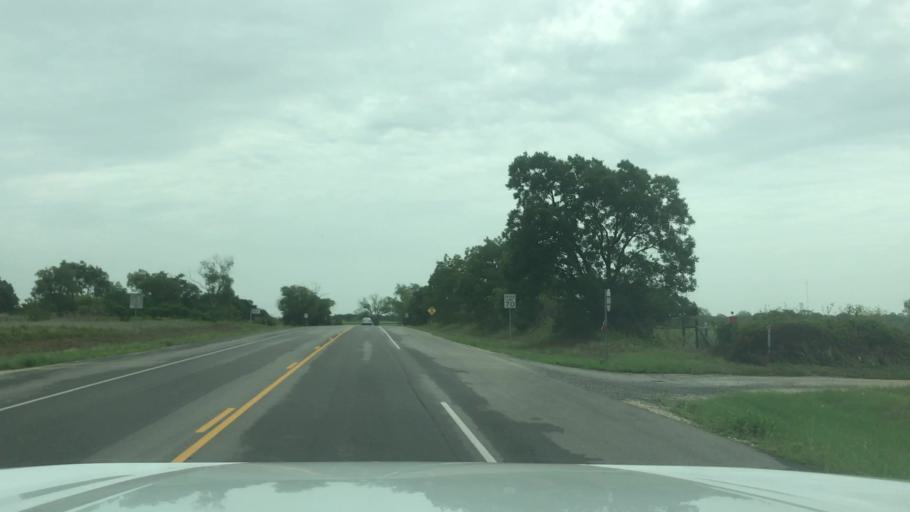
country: US
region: Texas
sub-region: Eastland County
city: Gorman
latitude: 32.2219
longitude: -98.6861
